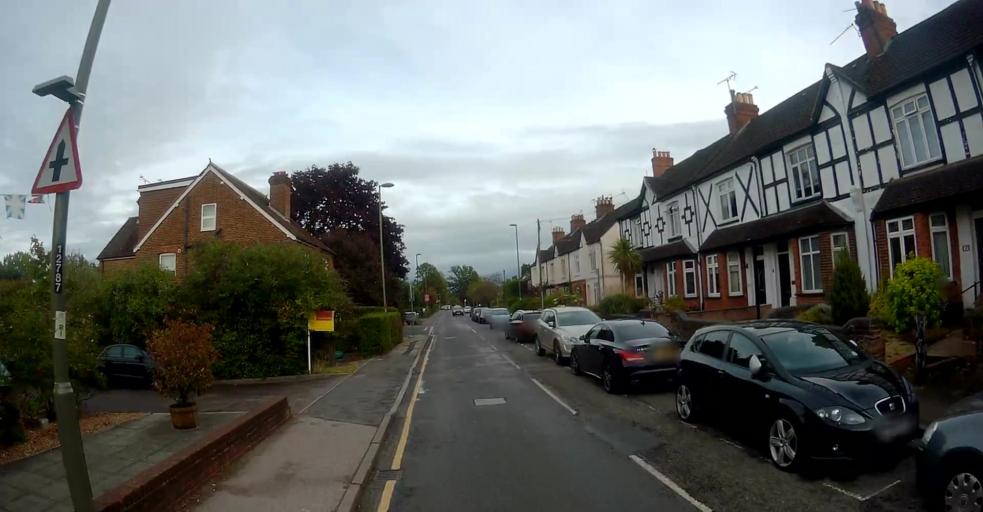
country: GB
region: England
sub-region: Surrey
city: Pirbright
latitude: 51.3044
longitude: -0.6355
